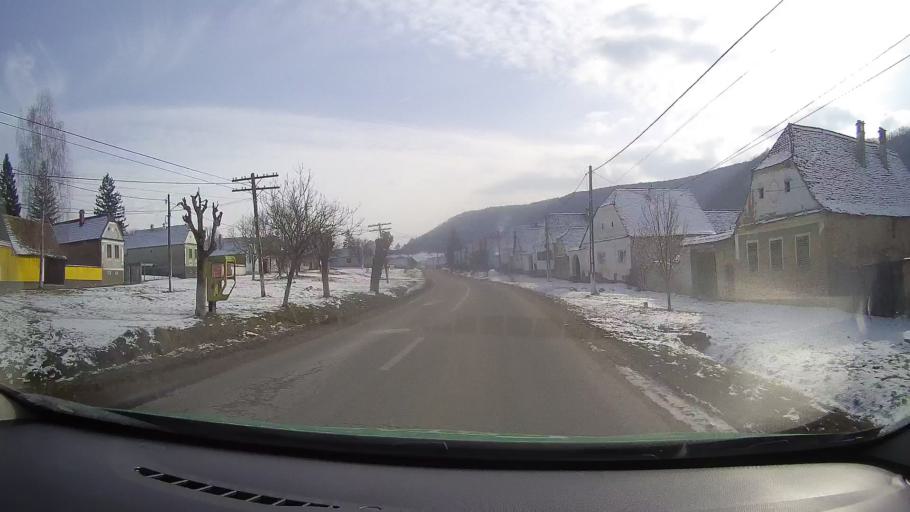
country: RO
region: Mures
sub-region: Comuna Apold
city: Saes
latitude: 46.1521
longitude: 24.7706
